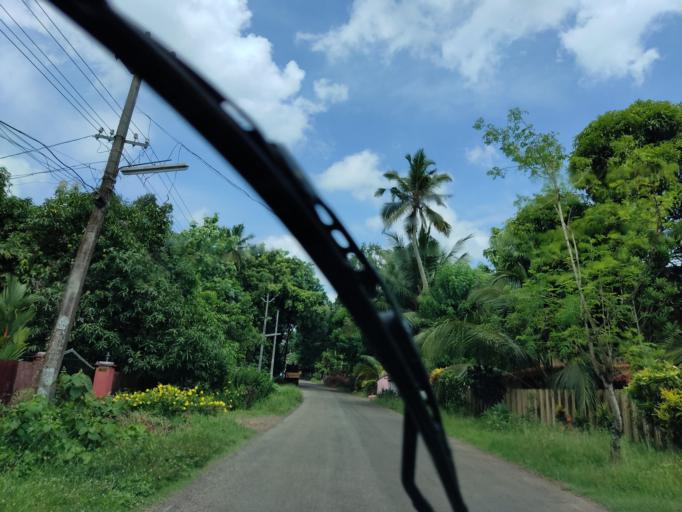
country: IN
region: Kerala
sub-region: Alappuzha
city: Mavelikara
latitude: 9.2539
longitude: 76.5677
